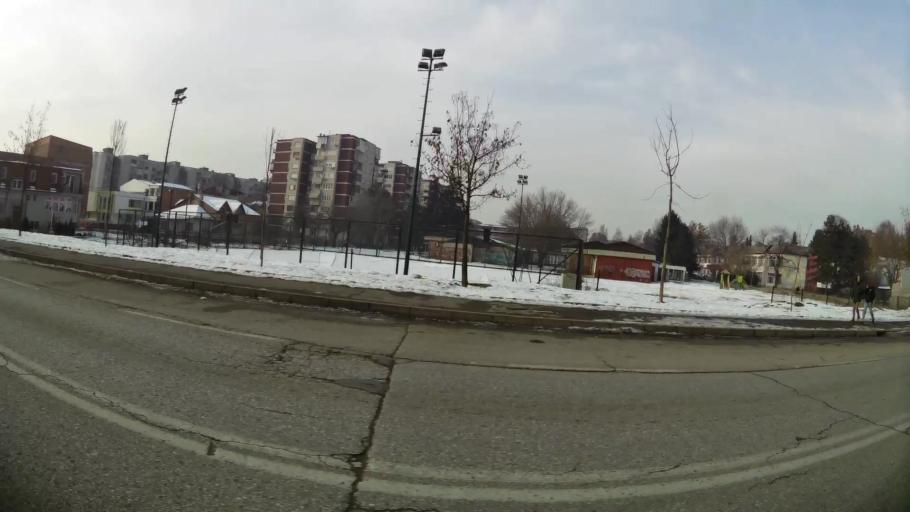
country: MK
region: Cair
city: Cair
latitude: 42.0192
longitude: 21.4351
